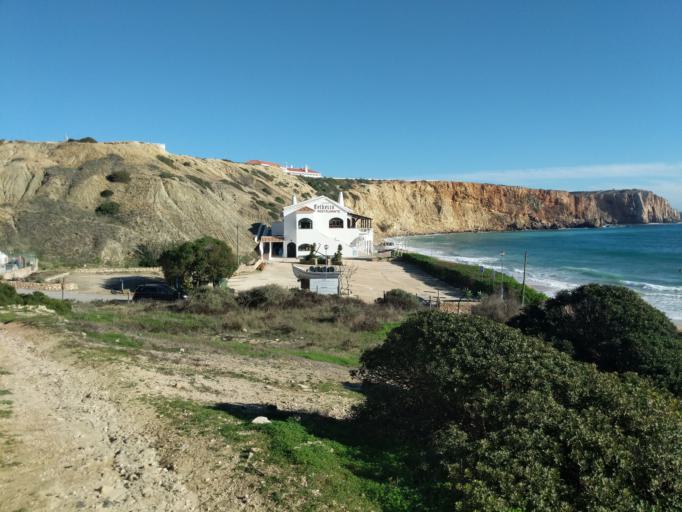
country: PT
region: Faro
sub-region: Vila do Bispo
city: Sagres
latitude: 37.0062
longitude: -8.9386
